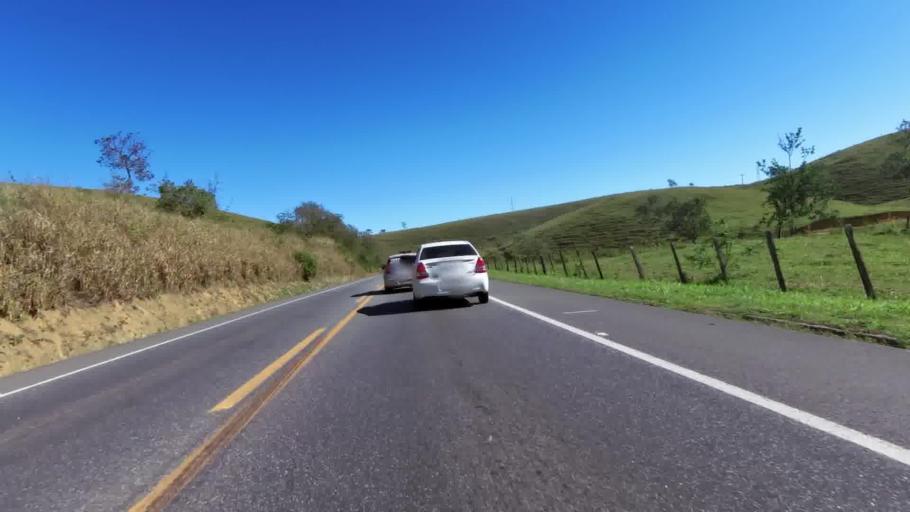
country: BR
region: Espirito Santo
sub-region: Alfredo Chaves
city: Alfredo Chaves
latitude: -20.6915
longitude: -40.6928
